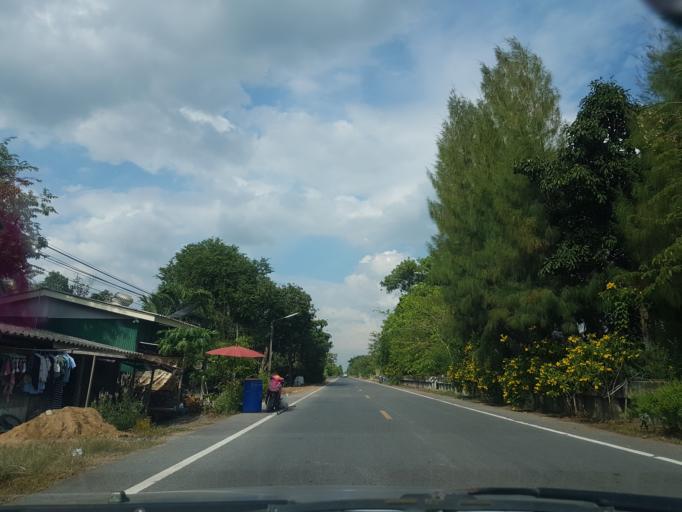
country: TH
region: Pathum Thani
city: Nong Suea
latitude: 14.1645
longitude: 100.8915
